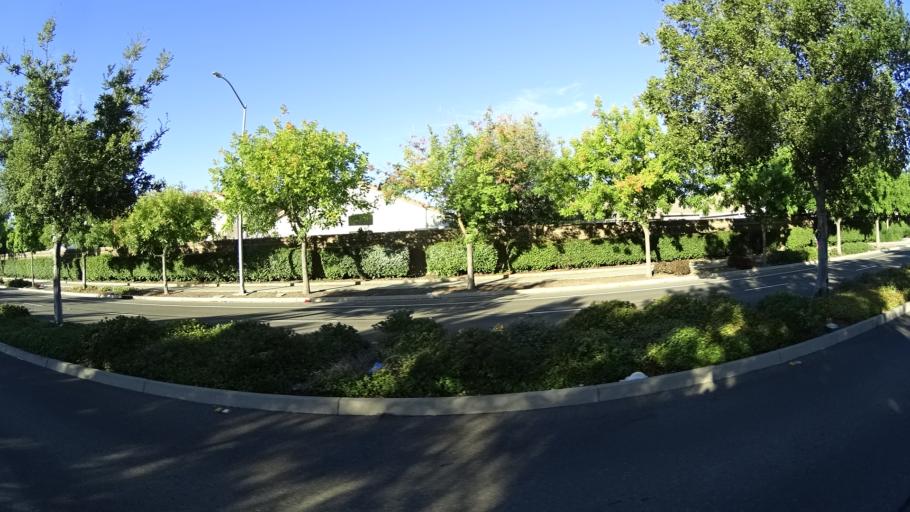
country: US
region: California
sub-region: Sacramento County
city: Laguna
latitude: 38.4455
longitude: -121.3922
